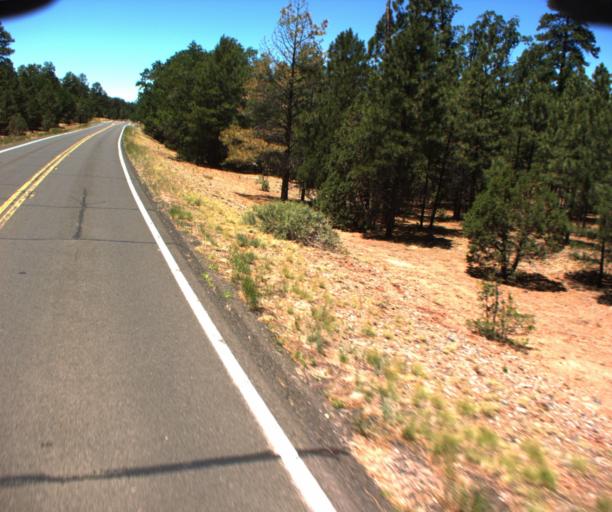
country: US
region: Arizona
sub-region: Gila County
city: Star Valley
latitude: 34.6278
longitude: -111.1234
